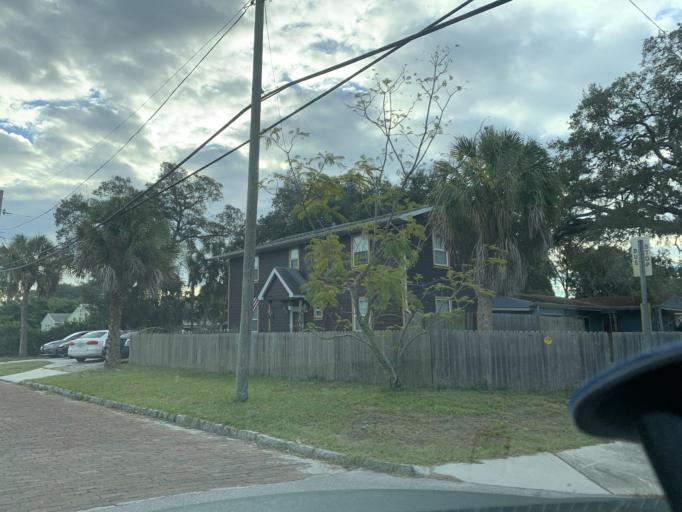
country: US
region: Florida
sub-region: Pinellas County
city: Gulfport
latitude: 27.7429
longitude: -82.6997
